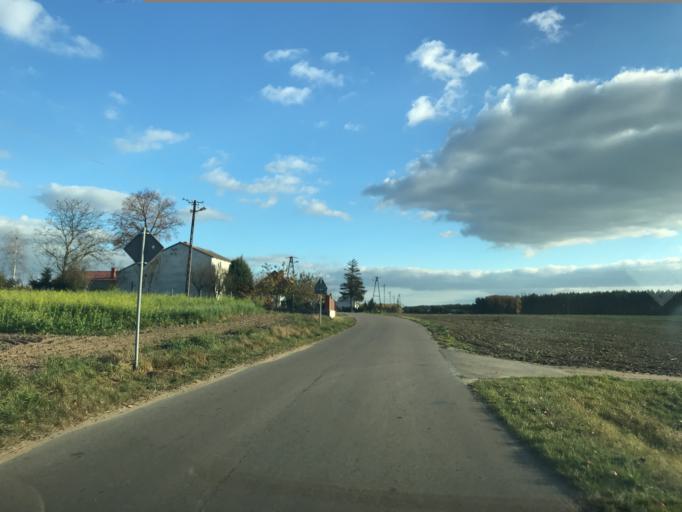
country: PL
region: Warmian-Masurian Voivodeship
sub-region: Powiat dzialdowski
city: Rybno
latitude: 53.3810
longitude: 19.8192
